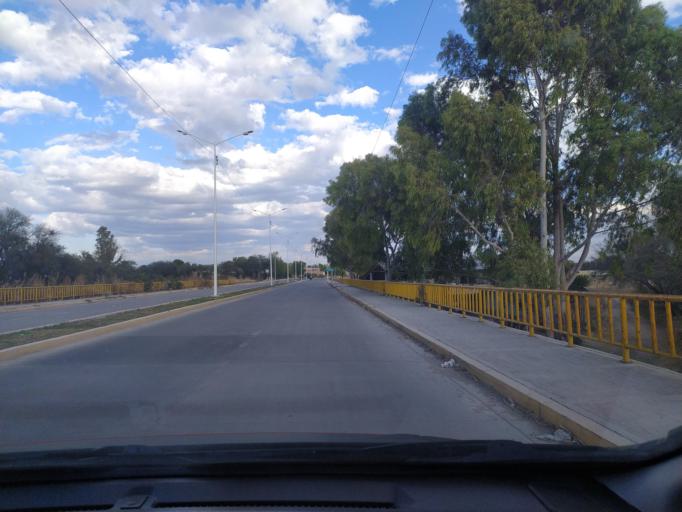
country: LA
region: Oudomxai
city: Muang La
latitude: 21.0184
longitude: 101.8379
